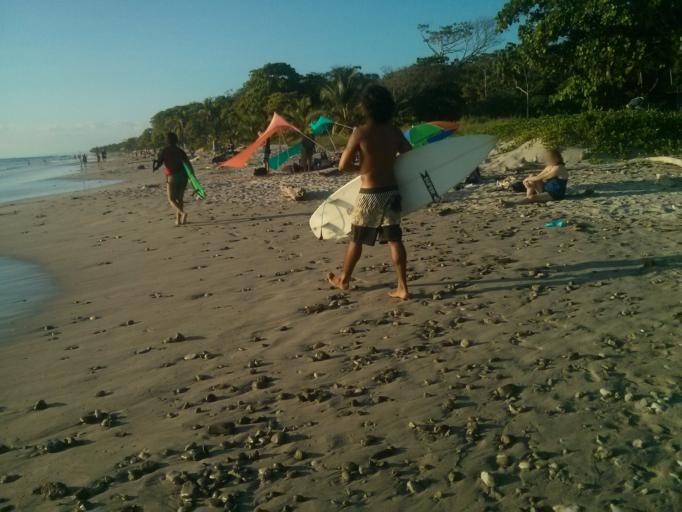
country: CR
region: Guanacaste
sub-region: Canton de Nandayure
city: Bejuco
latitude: 9.6270
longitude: -85.1526
